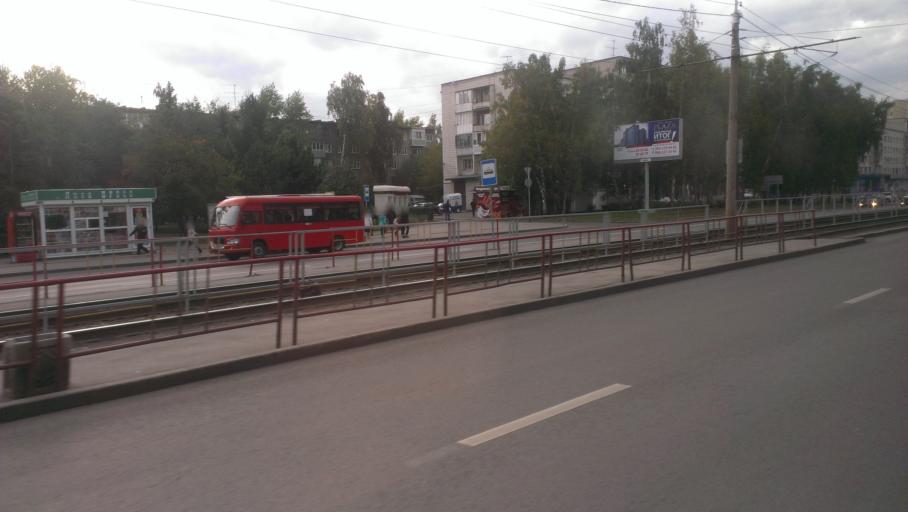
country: RU
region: Altai Krai
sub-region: Gorod Barnaulskiy
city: Barnaul
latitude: 53.3452
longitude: 83.7660
